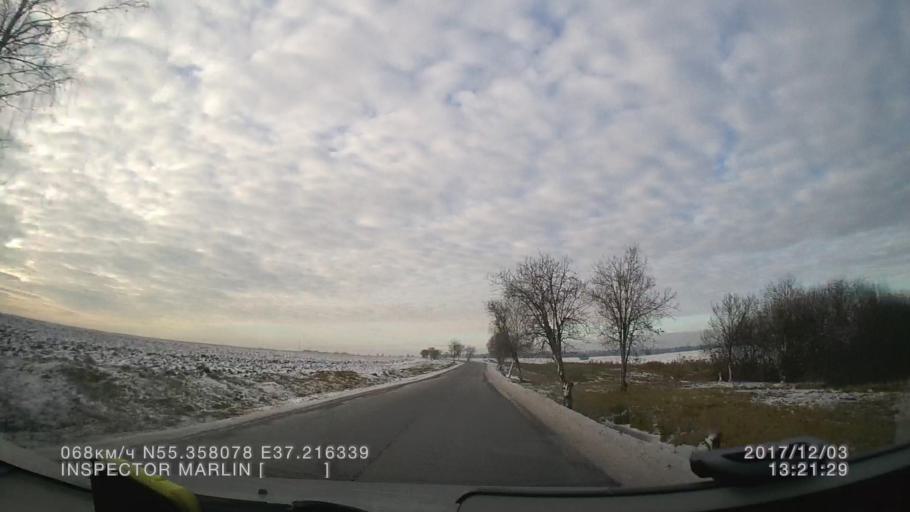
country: RU
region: Moskovskaya
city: Troitsk
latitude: 55.3581
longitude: 37.2163
